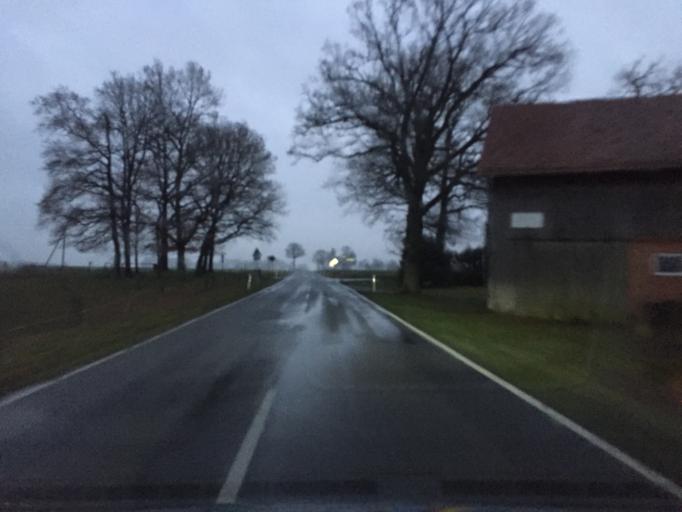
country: DE
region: Lower Saxony
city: Sudwalde
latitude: 52.8124
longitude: 8.8409
